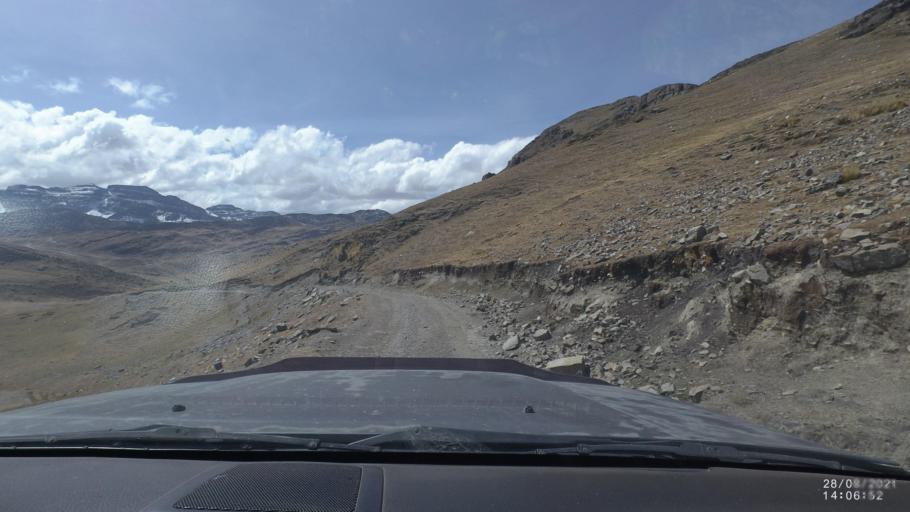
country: BO
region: Cochabamba
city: Sipe Sipe
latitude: -17.2682
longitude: -66.3838
